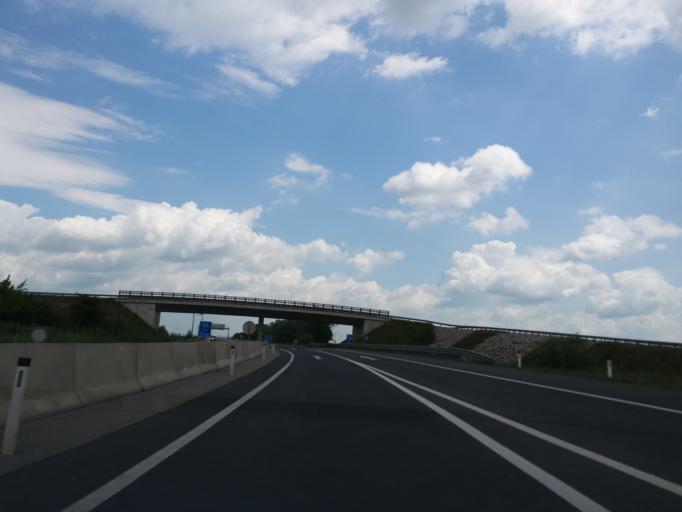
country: AT
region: Burgenland
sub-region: Politischer Bezirk Neusiedl am See
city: Parndorf
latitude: 48.0209
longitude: 16.8402
